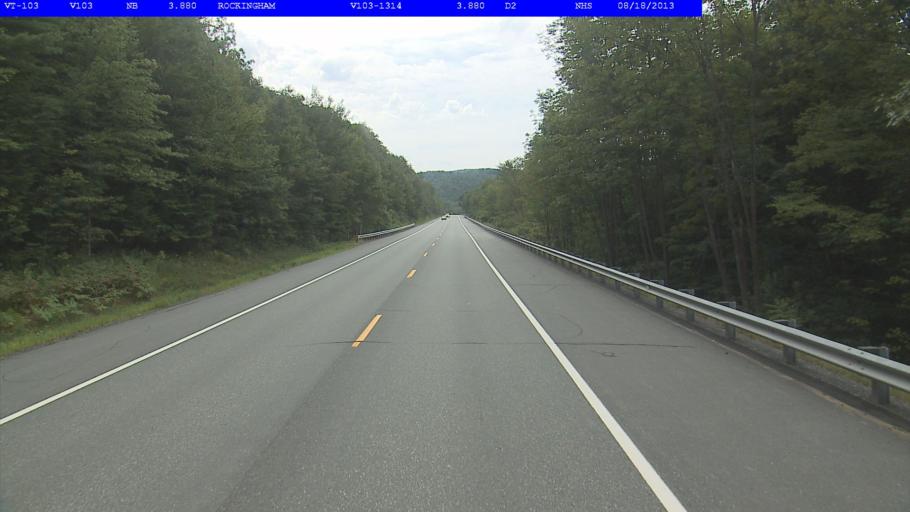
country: US
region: Vermont
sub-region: Windham County
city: Rockingham
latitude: 43.2046
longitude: -72.5247
